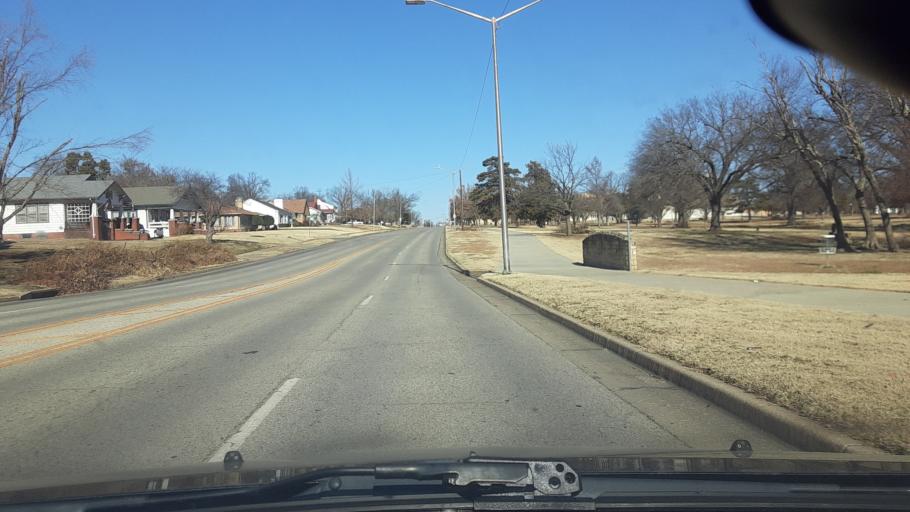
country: US
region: Oklahoma
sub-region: Kay County
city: Ponca City
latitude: 36.7106
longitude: -97.0783
